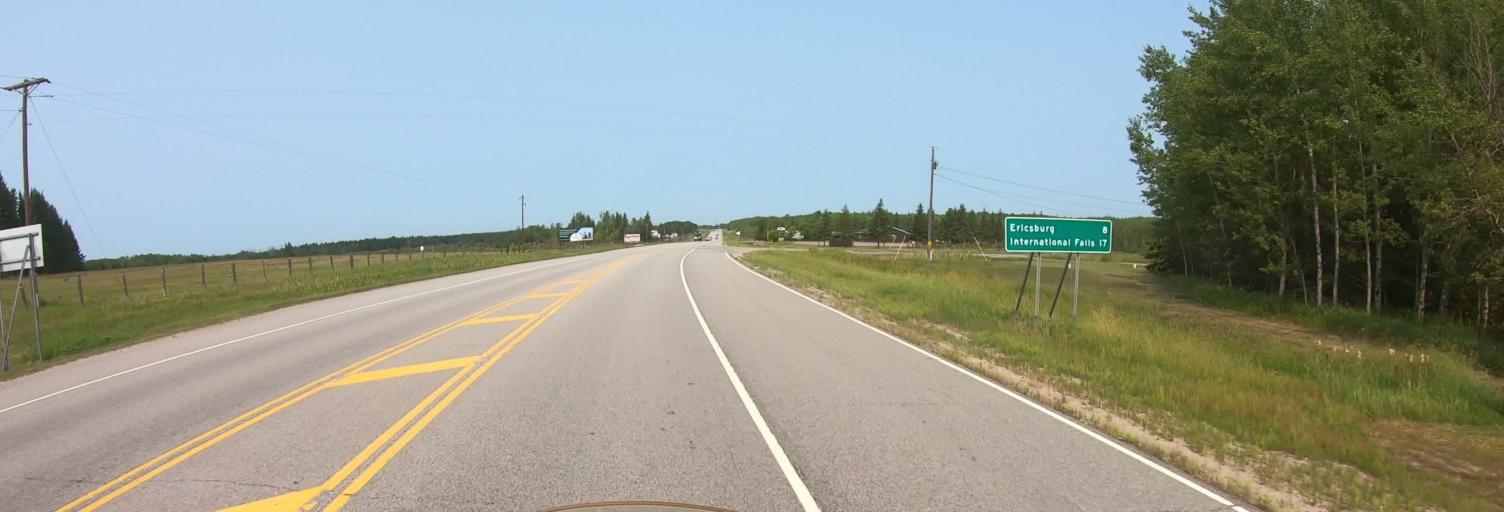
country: CA
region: Ontario
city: Fort Frances
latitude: 48.4120
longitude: -93.2044
